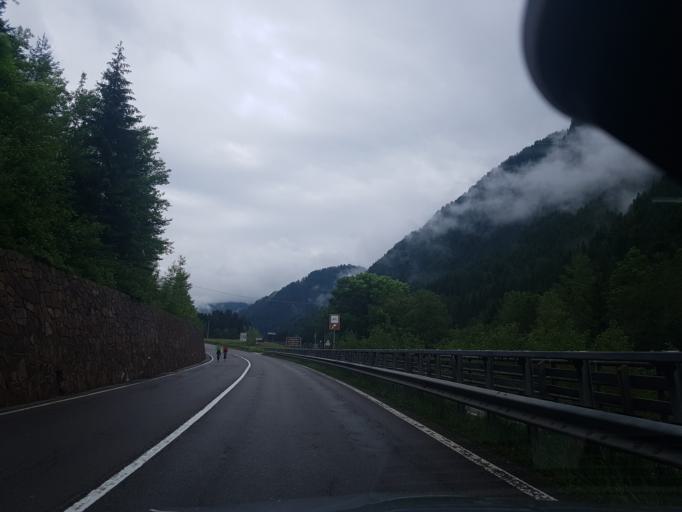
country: IT
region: Trentino-Alto Adige
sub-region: Bolzano
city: Ortisei
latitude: 46.5671
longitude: 11.6866
